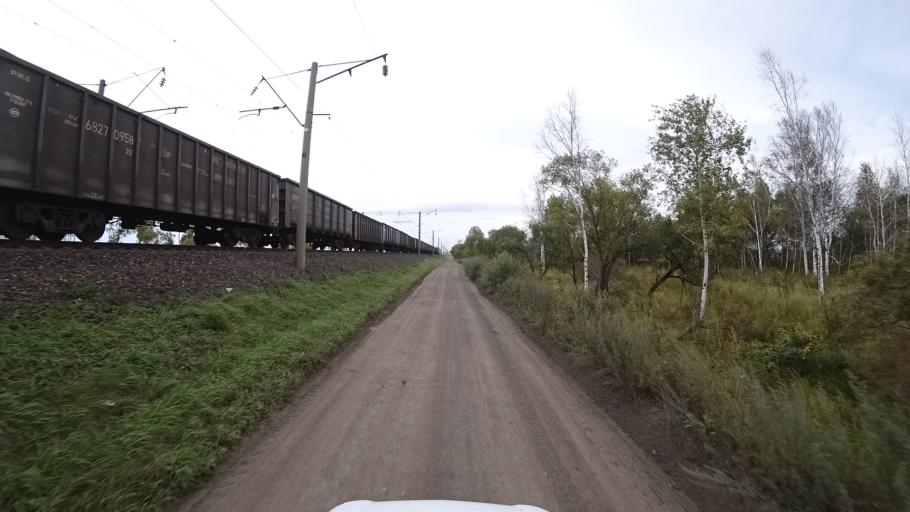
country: RU
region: Amur
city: Arkhara
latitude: 49.3610
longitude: 130.1489
